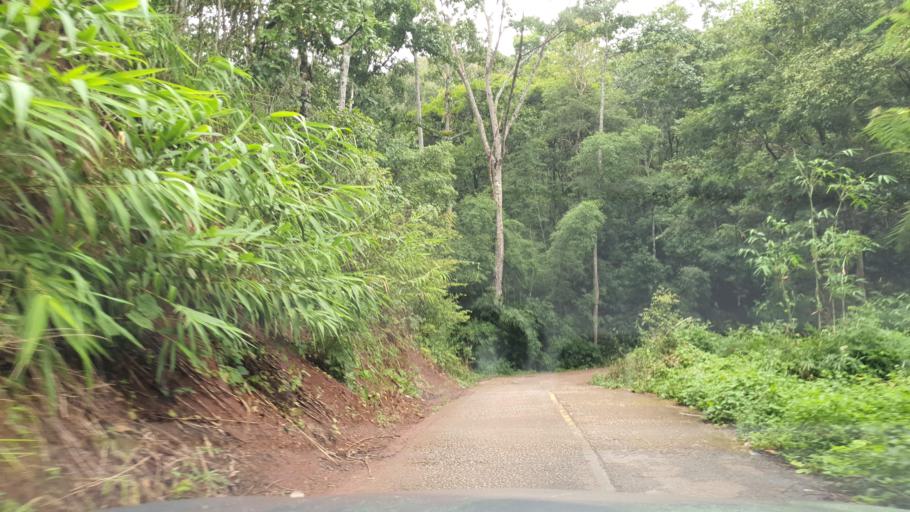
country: TH
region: Chiang Mai
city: Mae Taeng
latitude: 19.2183
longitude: 98.9256
